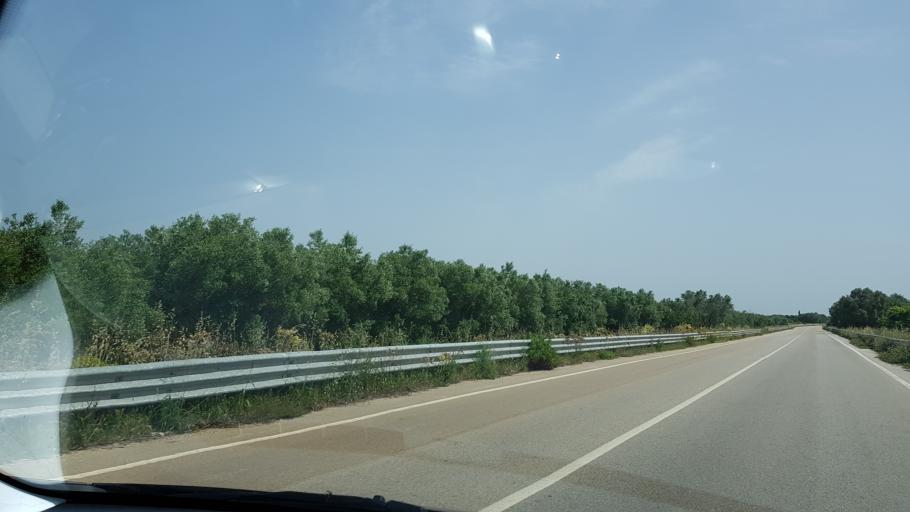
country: IT
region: Apulia
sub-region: Provincia di Brindisi
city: San Pancrazio Salentino
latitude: 40.4776
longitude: 17.8366
